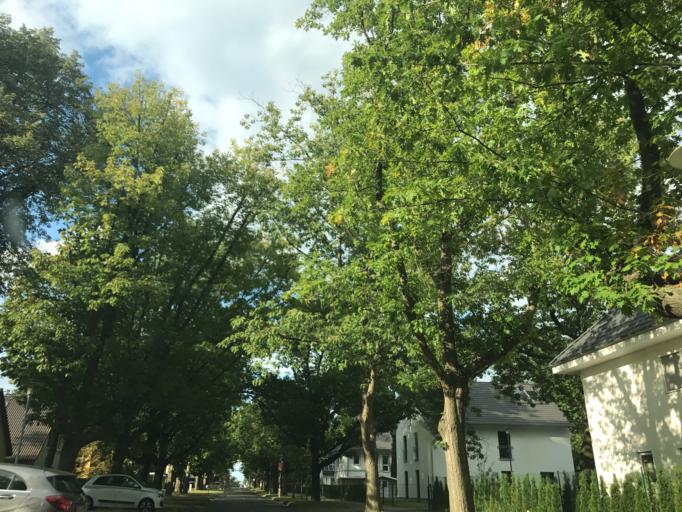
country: DE
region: Brandenburg
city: Dallgow-Doeberitz
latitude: 52.5384
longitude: 13.0548
